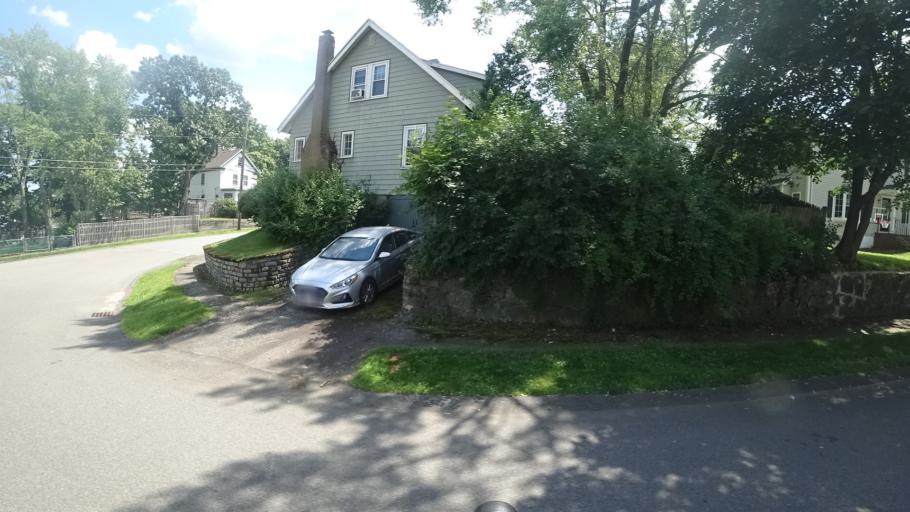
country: US
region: Massachusetts
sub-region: Norfolk County
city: Dedham
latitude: 42.2730
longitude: -71.1777
